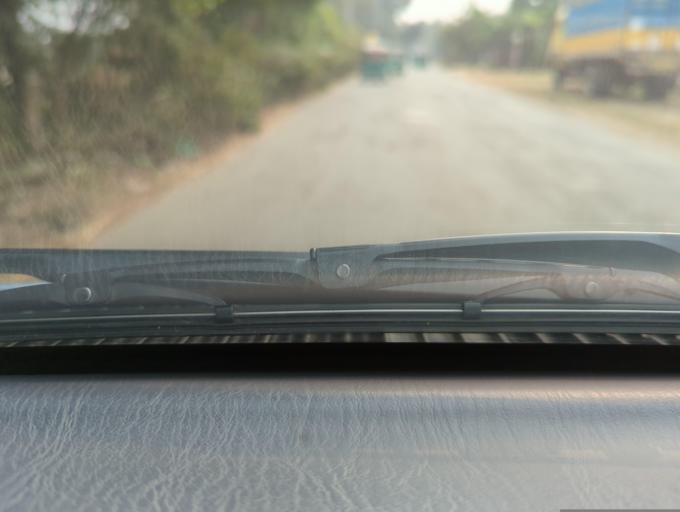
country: BD
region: Sylhet
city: Maulavi Bazar
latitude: 24.4950
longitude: 91.7468
